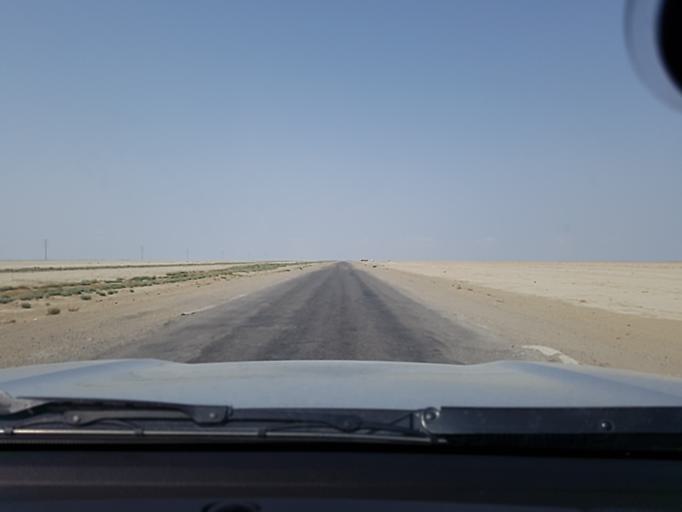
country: TM
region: Balkan
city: Gumdag
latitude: 38.7279
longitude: 54.4913
